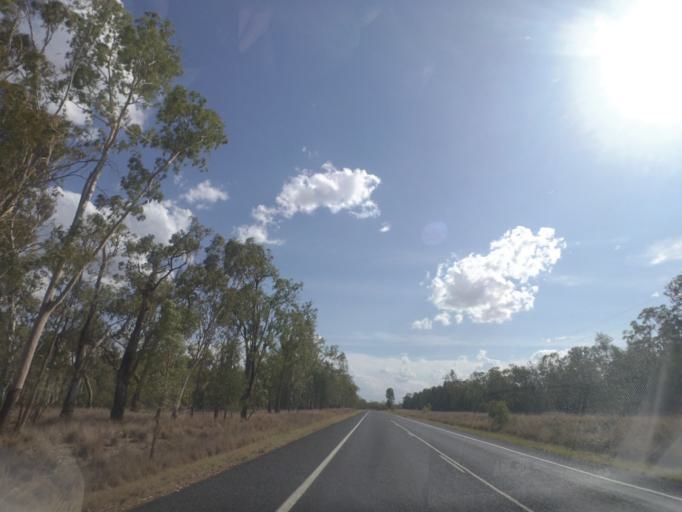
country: AU
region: New South Wales
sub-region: Moree Plains
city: Boggabilla
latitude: -28.5393
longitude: 150.8874
